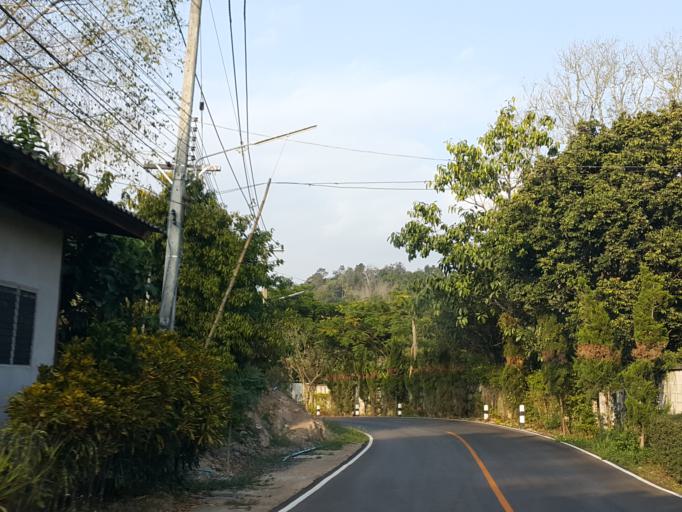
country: TH
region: Chiang Mai
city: Mae On
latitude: 18.8817
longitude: 99.2656
